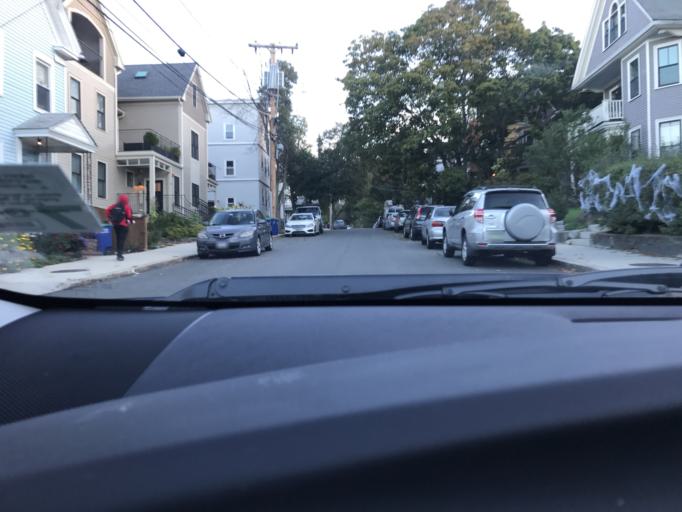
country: US
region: Massachusetts
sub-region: Middlesex County
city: Somerville
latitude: 42.3874
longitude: -71.1144
